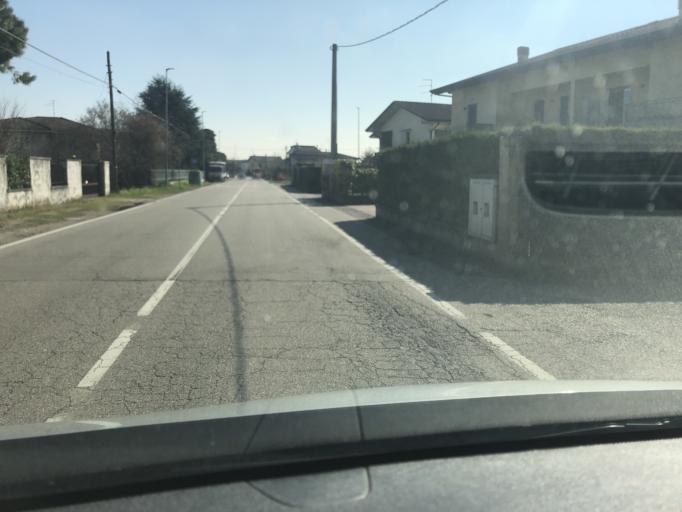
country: IT
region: Veneto
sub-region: Provincia di Verona
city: Villafranca di Verona
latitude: 45.3634
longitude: 10.8375
